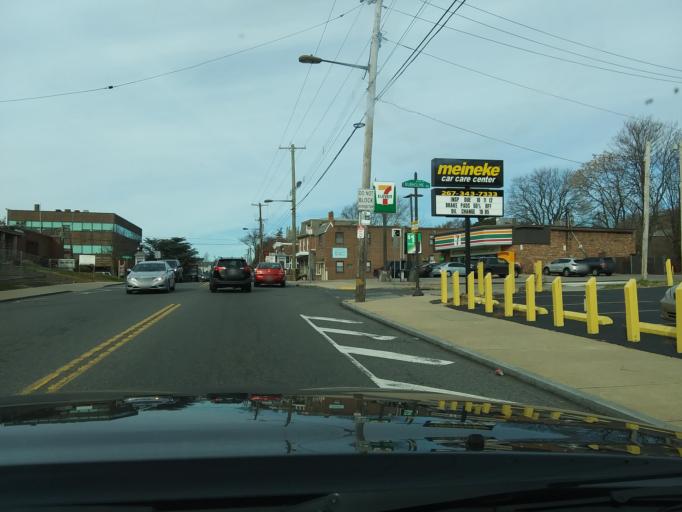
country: US
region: Pennsylvania
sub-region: Montgomery County
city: Rockledge
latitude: 40.0781
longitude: -75.0862
